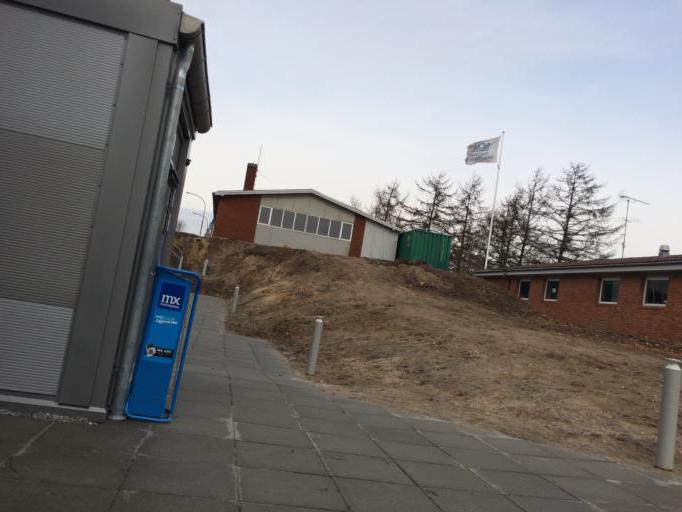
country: DK
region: Capital Region
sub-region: Hoje-Taastrup Kommune
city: Taastrup
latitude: 55.6514
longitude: 12.3167
